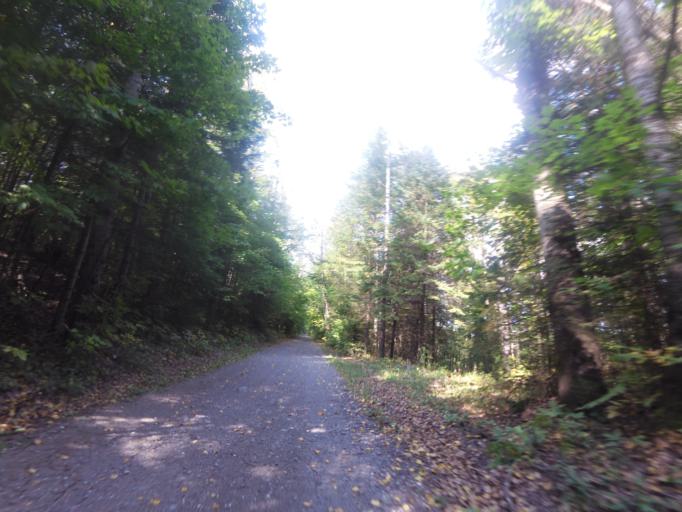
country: CA
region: Ontario
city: Renfrew
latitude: 45.1392
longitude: -76.6859
